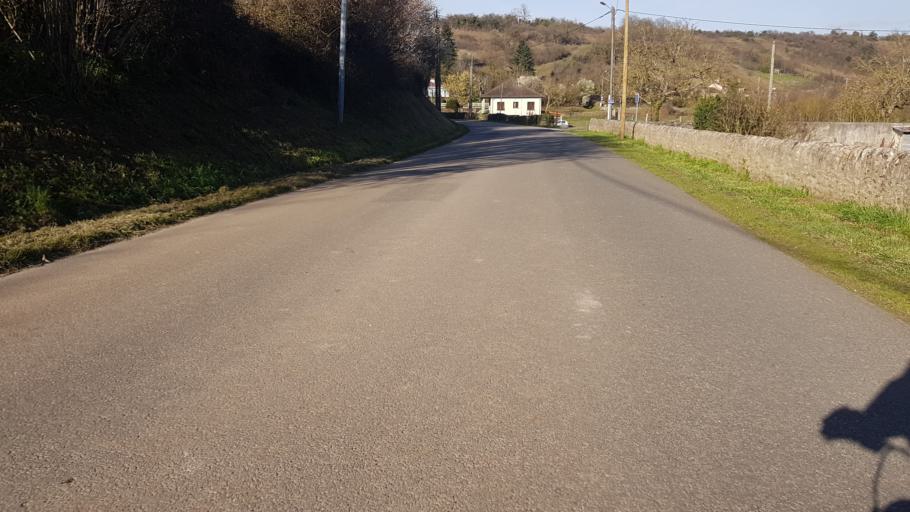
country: FR
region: Poitou-Charentes
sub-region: Departement de la Vienne
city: Migne-Auxances
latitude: 46.6404
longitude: 0.3381
